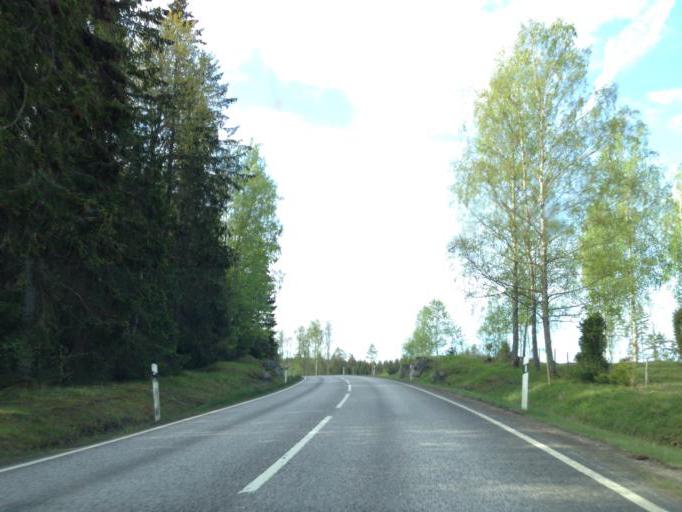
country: SE
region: Soedermanland
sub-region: Nykopings Kommun
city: Stigtomta
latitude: 58.9461
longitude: 16.8463
